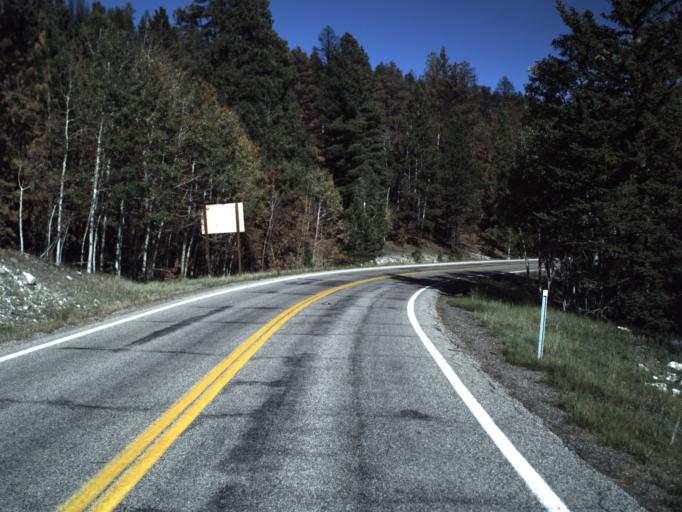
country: US
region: Utah
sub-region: Iron County
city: Parowan
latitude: 37.6544
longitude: -112.7032
